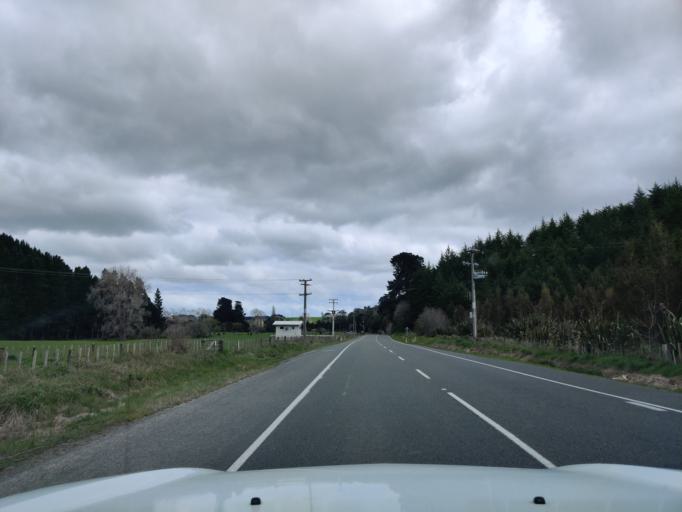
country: NZ
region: Manawatu-Wanganui
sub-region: Wanganui District
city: Wanganui
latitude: -39.8475
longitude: 175.1272
